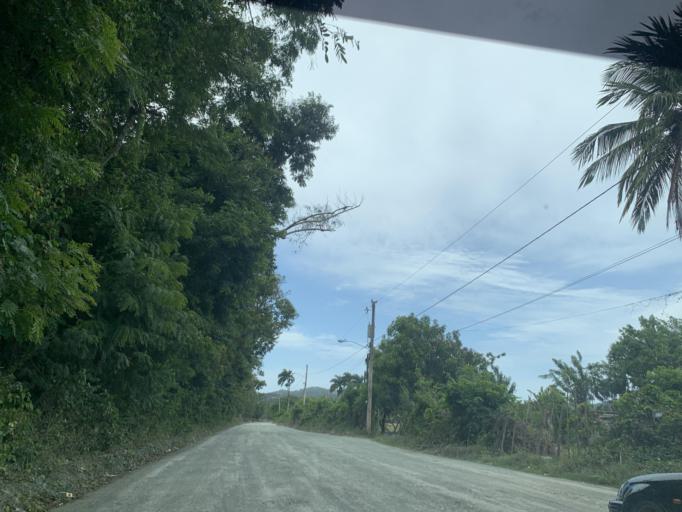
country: DO
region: Puerto Plata
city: Imbert
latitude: 19.8203
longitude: -70.7809
